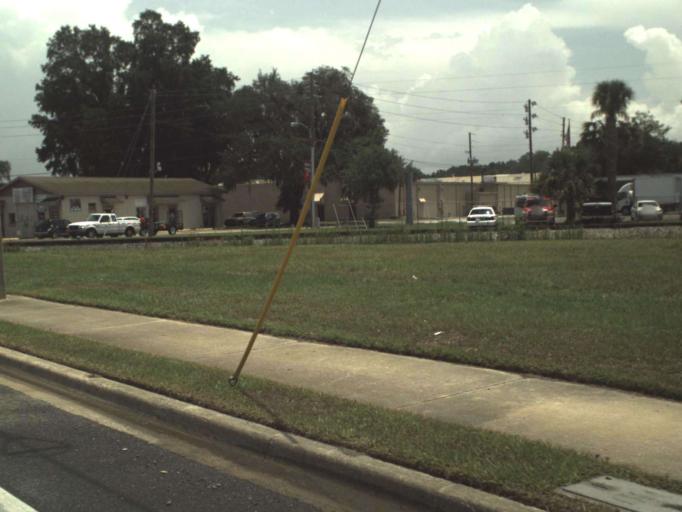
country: US
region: Florida
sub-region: Sumter County
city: Wildwood
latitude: 28.8578
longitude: -82.0431
